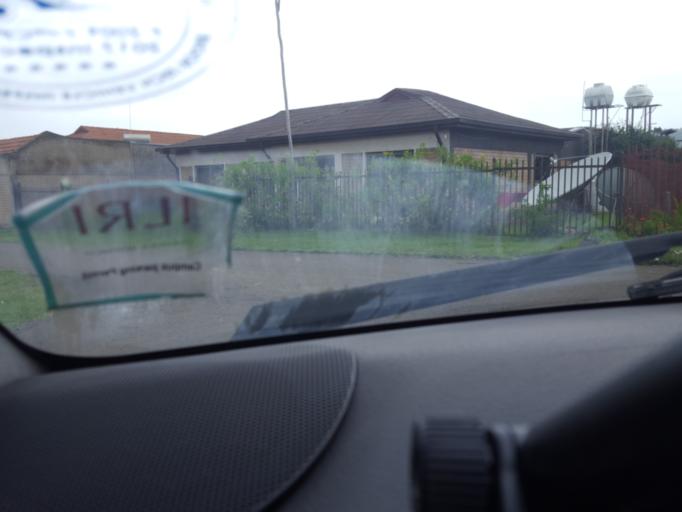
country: ET
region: Adis Abeba
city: Addis Ababa
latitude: 9.0738
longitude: 38.8852
